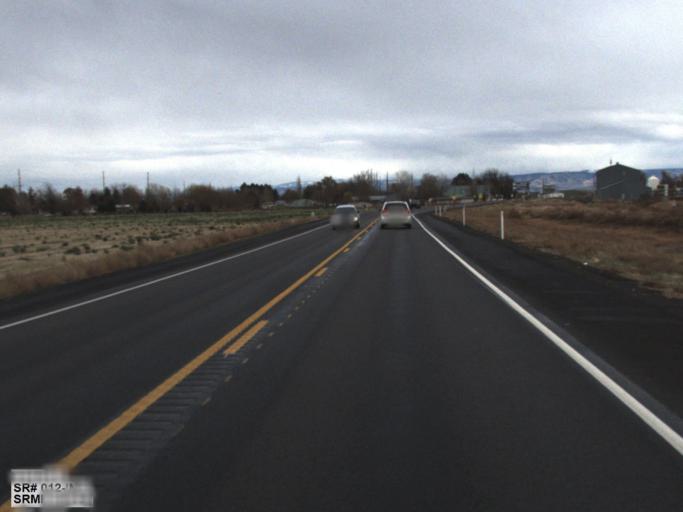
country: US
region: Washington
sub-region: Walla Walla County
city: Garrett
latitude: 46.0415
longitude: -118.6816
